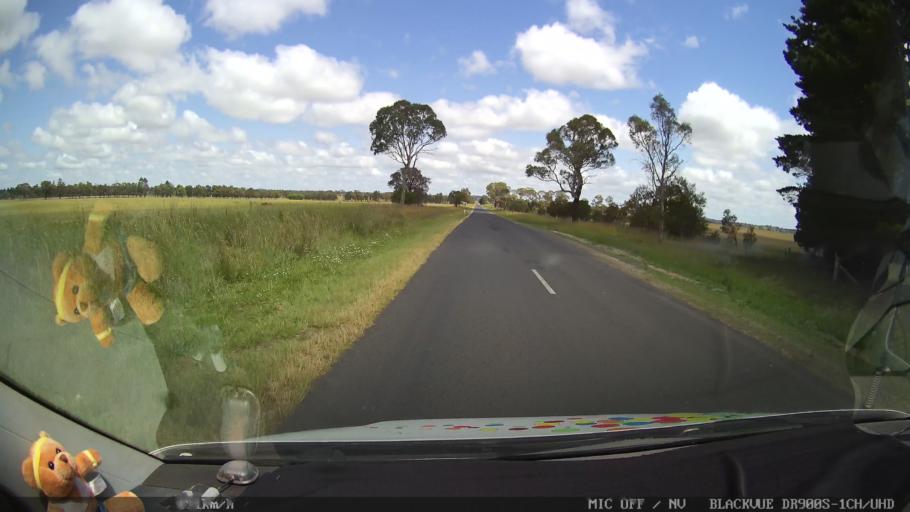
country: AU
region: New South Wales
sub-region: Glen Innes Severn
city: Glen Innes
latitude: -29.6914
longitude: 151.7100
